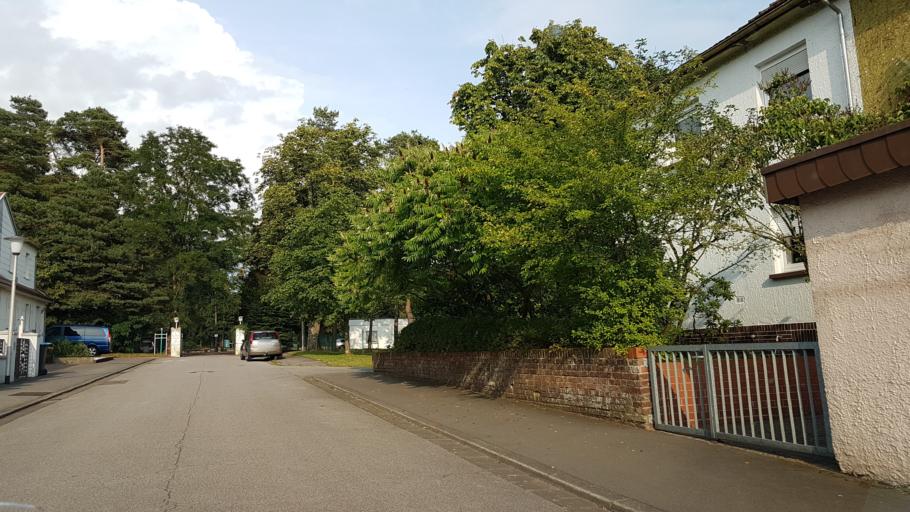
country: DE
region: Saarland
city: Homburg
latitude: 49.3163
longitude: 7.3505
